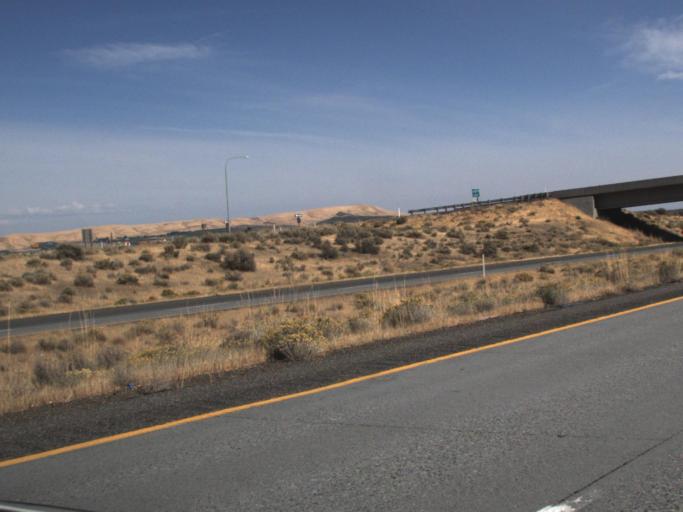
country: US
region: Washington
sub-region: Benton County
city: Benton City
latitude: 46.2640
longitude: -119.5358
